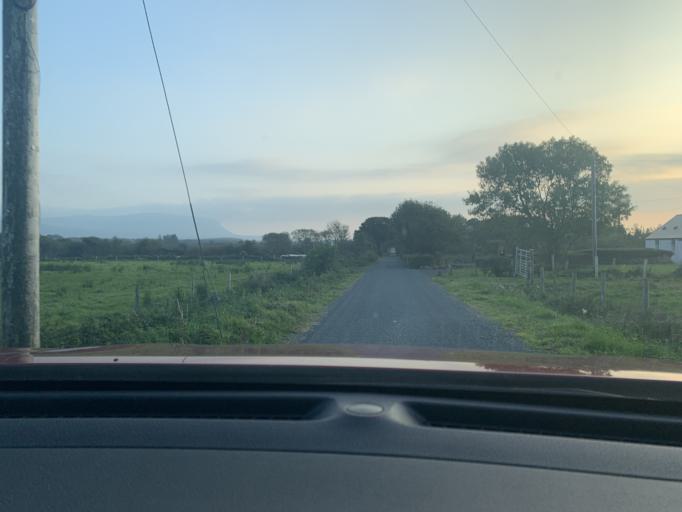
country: IE
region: Connaught
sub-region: County Leitrim
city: Kinlough
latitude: 54.4347
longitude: -8.4359
